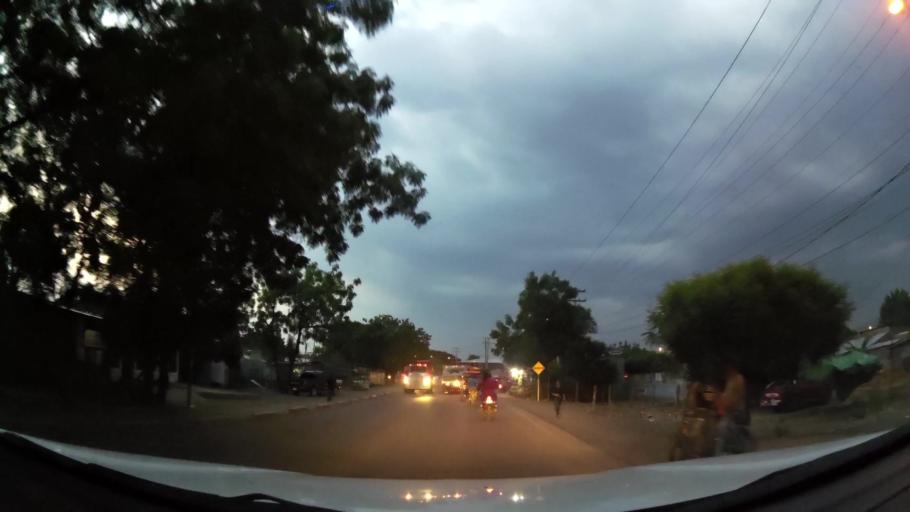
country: NI
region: Matagalpa
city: Ciudad Dario
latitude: 12.8555
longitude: -86.0996
